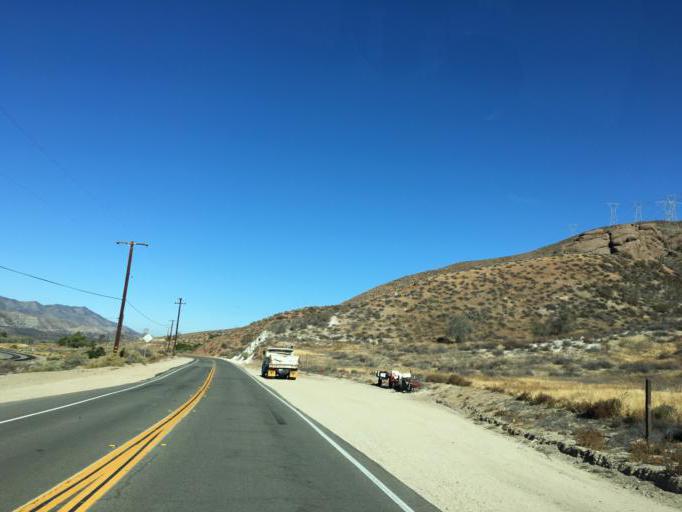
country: US
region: California
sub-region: Los Angeles County
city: Acton
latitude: 34.4391
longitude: -118.2237
